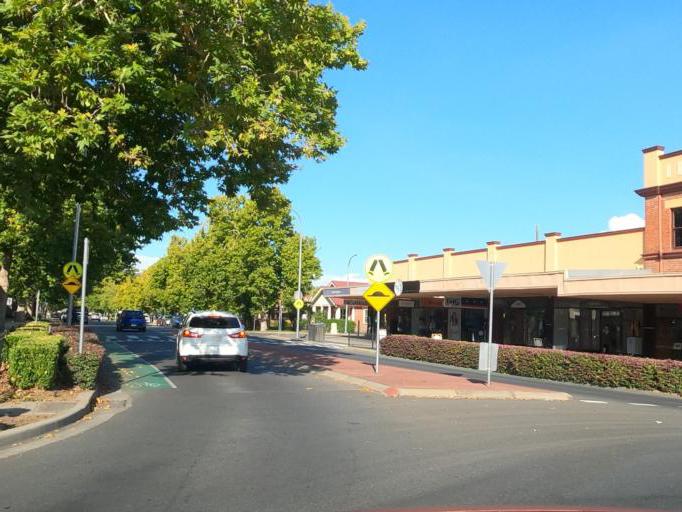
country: AU
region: New South Wales
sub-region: Albury Municipality
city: Albury
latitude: -36.0789
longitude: 146.9187
